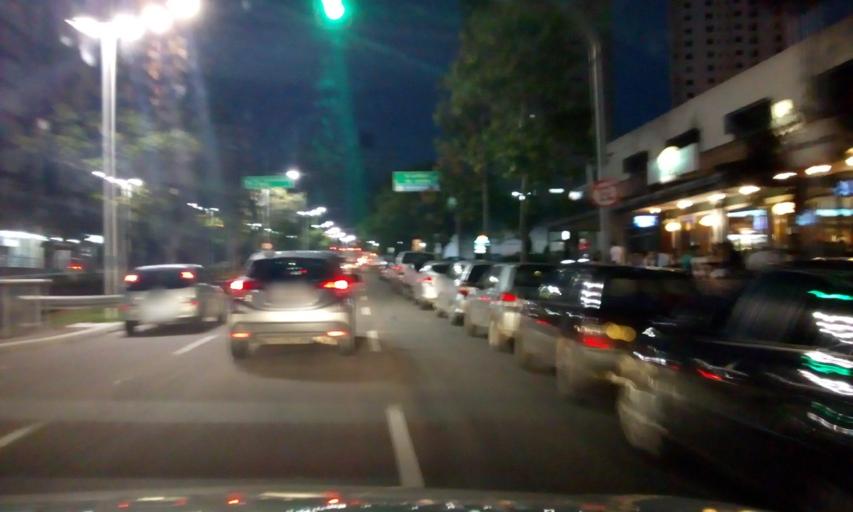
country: BR
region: Sao Paulo
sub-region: Jundiai
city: Jundiai
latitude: -23.1873
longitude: -46.8918
